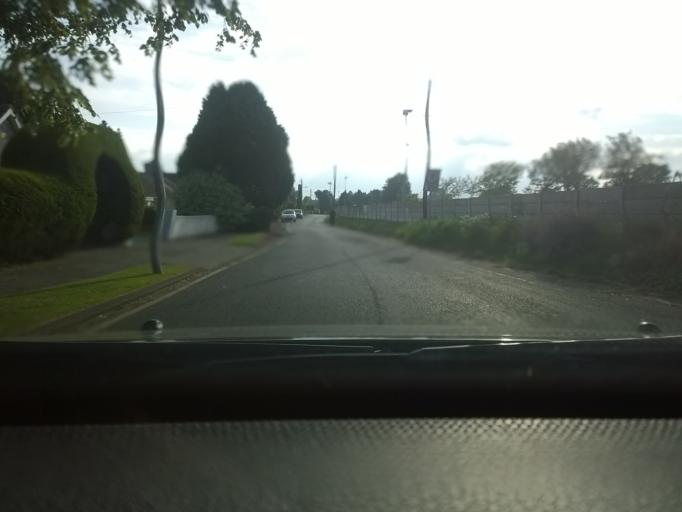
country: IE
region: Leinster
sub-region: Kildare
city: Kildare
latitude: 53.1621
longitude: -6.9089
